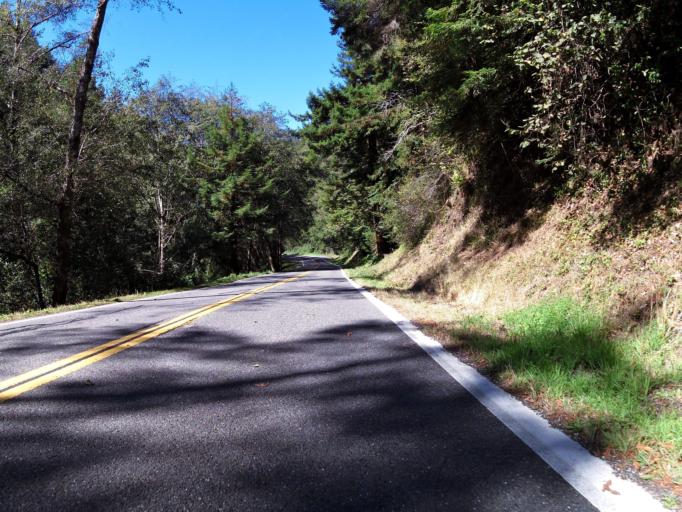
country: US
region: California
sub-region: Mendocino County
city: Fort Bragg
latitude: 39.7801
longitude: -123.8267
